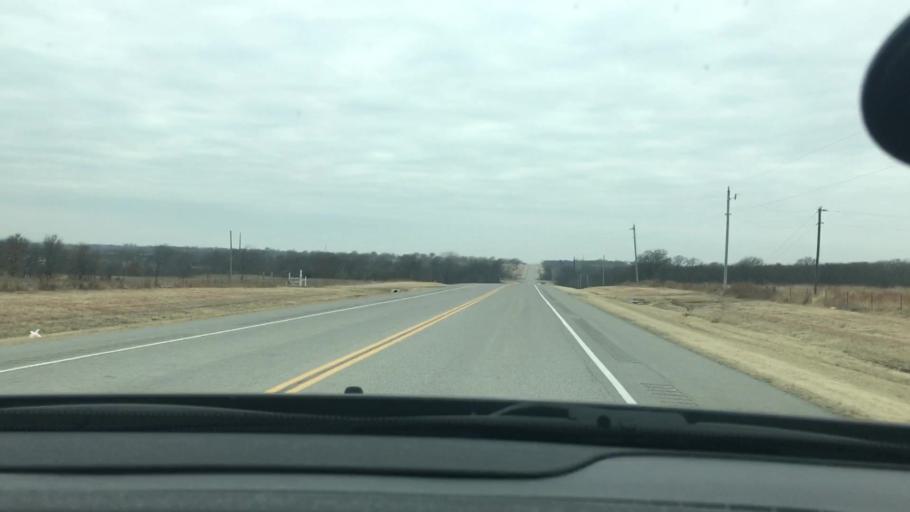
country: US
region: Oklahoma
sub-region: Carter County
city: Healdton
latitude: 34.4925
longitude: -97.3966
